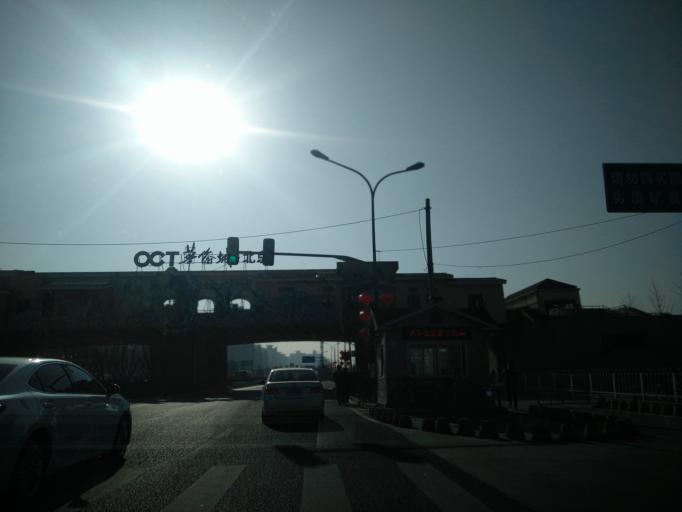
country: CN
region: Beijing
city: Longtan
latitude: 39.8662
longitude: 116.4939
